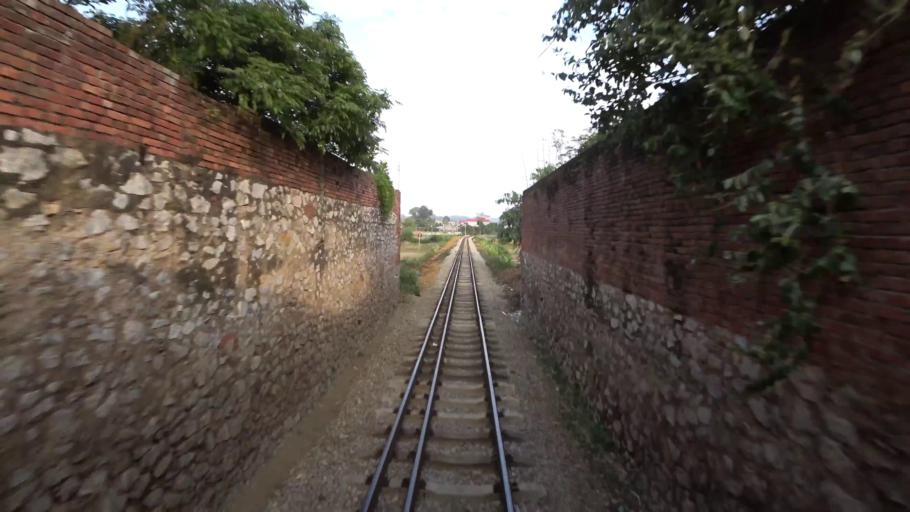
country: VN
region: Lang Son
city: Thi Tran Cao Loc
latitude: 21.8766
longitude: 106.7509
